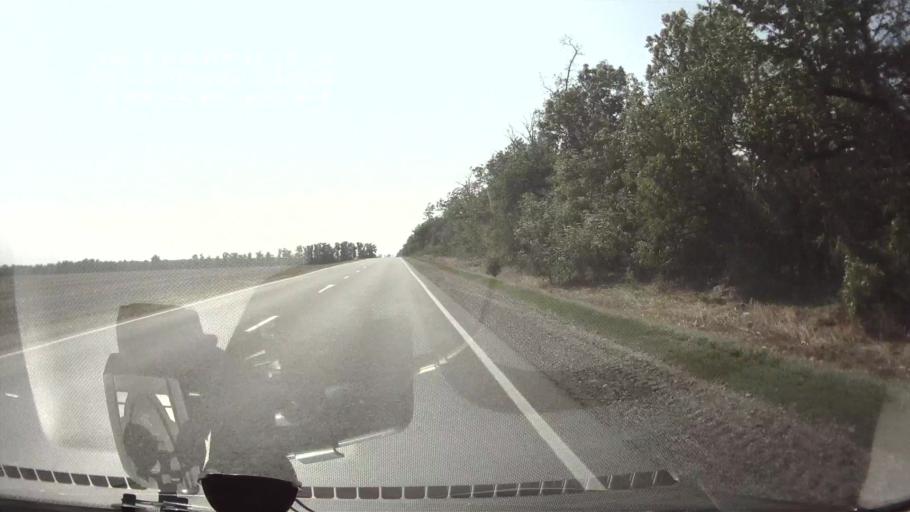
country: RU
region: Krasnodarskiy
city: Kavkazskaya
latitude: 45.5269
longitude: 40.6803
